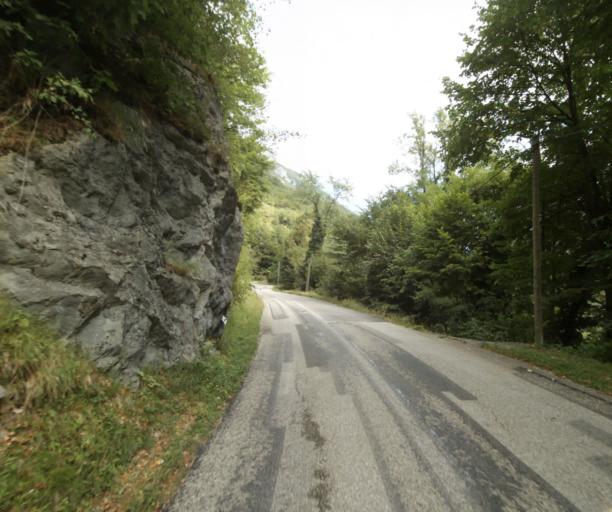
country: FR
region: Rhone-Alpes
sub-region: Departement de l'Isere
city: Saint-Egreve
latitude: 45.2705
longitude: 5.7019
